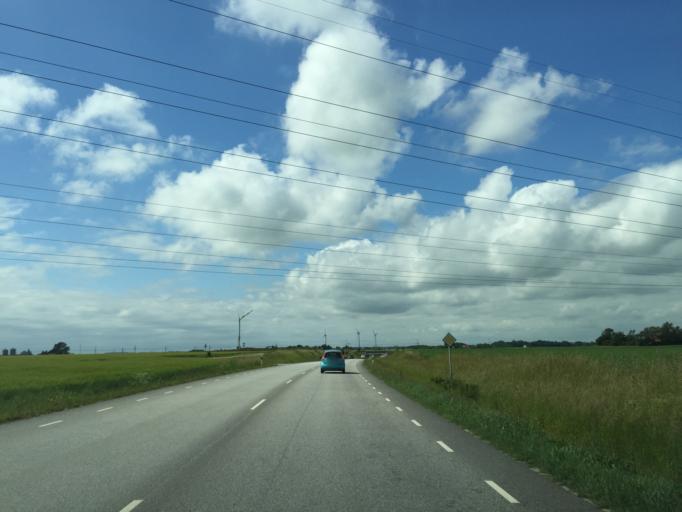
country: SE
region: Skane
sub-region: Staffanstorps Kommun
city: Hjaerup
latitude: 55.6827
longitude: 13.1623
